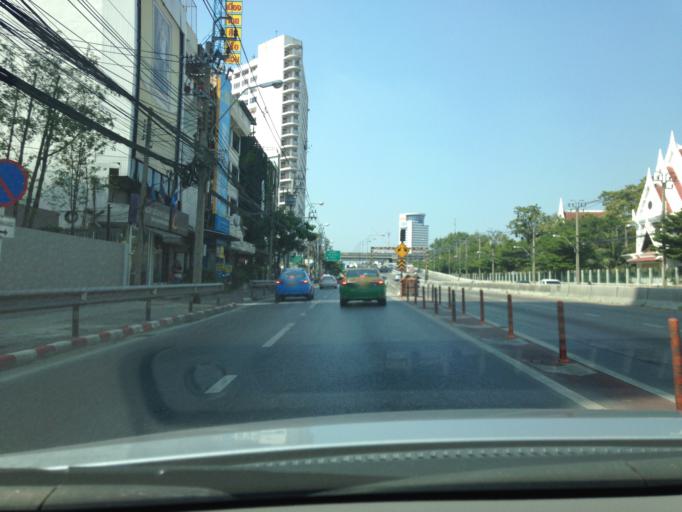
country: TH
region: Bangkok
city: Chatuchak
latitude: 13.8456
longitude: 100.5649
